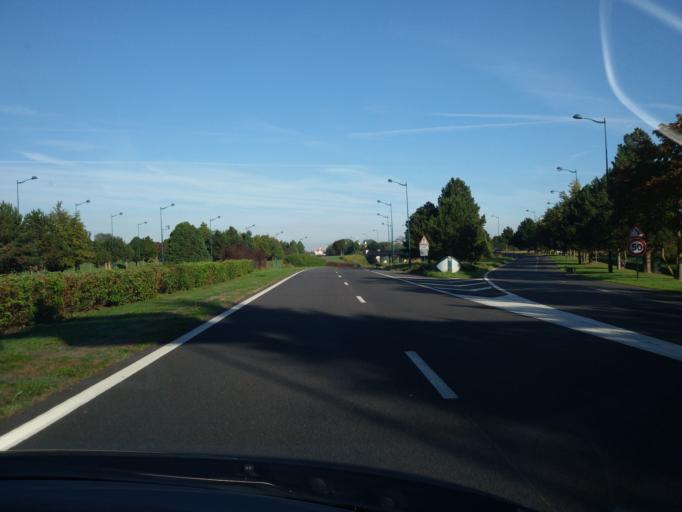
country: FR
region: Ile-de-France
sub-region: Departement de Seine-et-Marne
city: Serris
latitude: 48.8574
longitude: 2.7968
